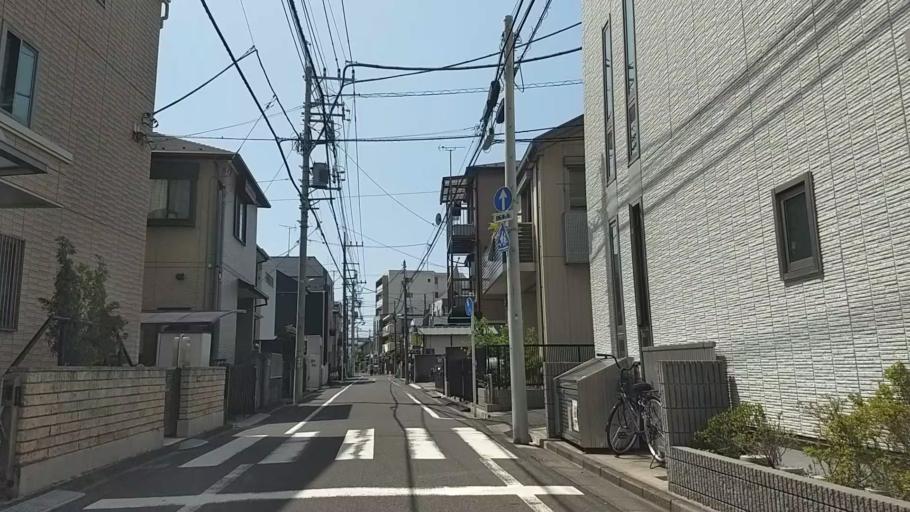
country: JP
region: Kanagawa
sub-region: Kawasaki-shi
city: Kawasaki
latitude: 35.5370
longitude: 139.6953
